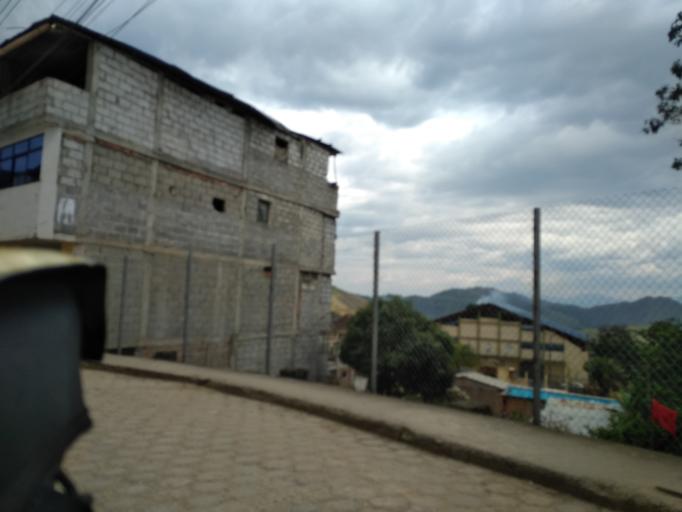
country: PE
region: Cajamarca
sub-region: Provincia de San Ignacio
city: Namballe
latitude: -4.8642
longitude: -79.1313
